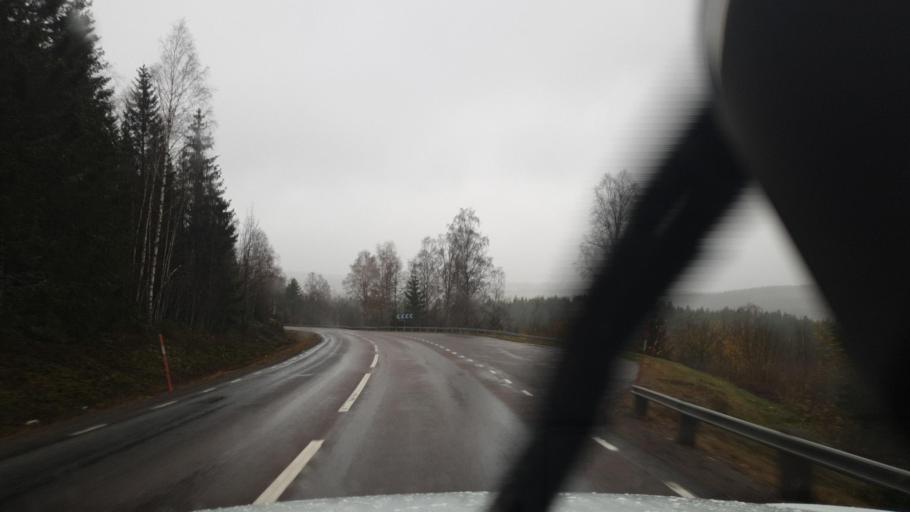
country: SE
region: Vaermland
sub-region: Sunne Kommun
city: Sunne
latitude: 59.6998
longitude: 13.1056
